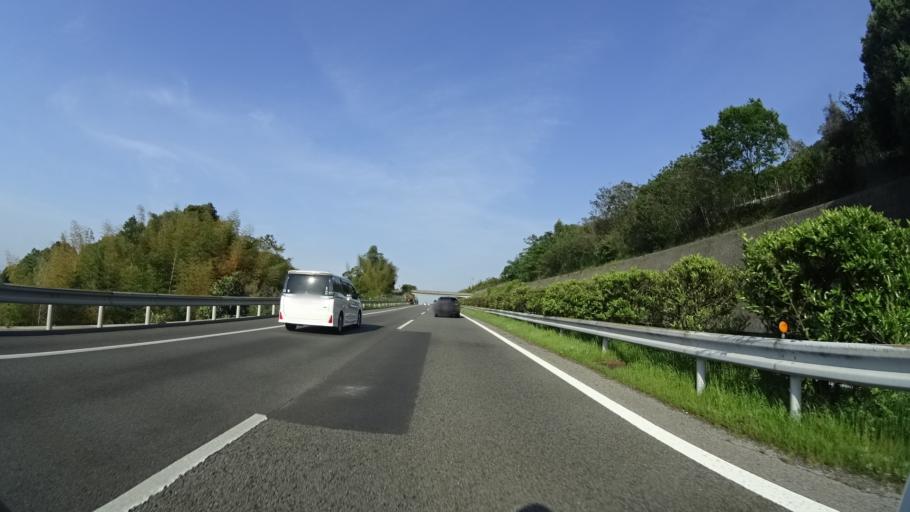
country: JP
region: Ehime
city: Niihama
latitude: 33.9143
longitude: 133.2787
